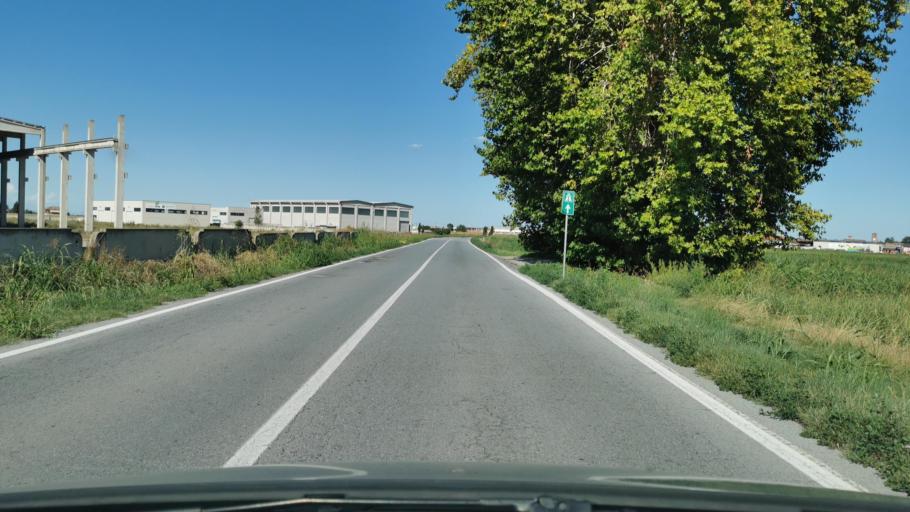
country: IT
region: Piedmont
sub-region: Provincia di Cuneo
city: Genola
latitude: 44.5848
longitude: 7.6474
